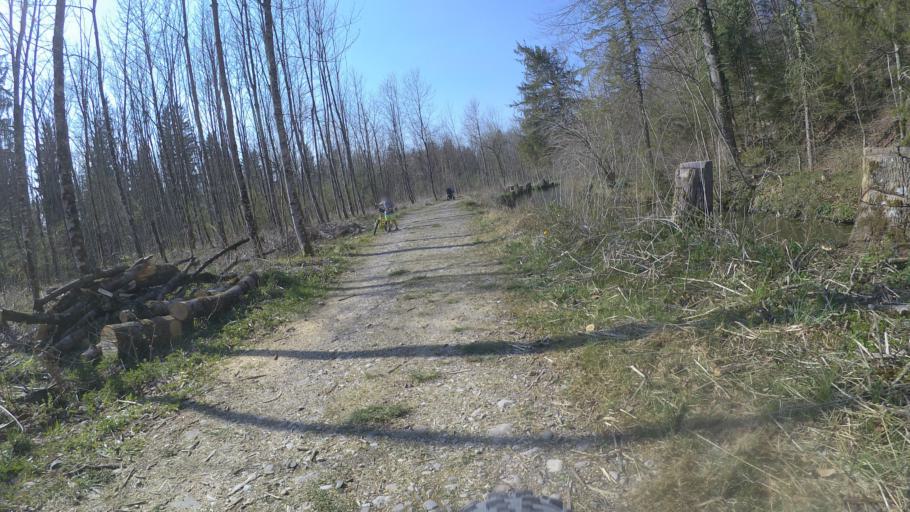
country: DE
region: Bavaria
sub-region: Upper Bavaria
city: Traunreut
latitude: 47.9585
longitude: 12.5788
